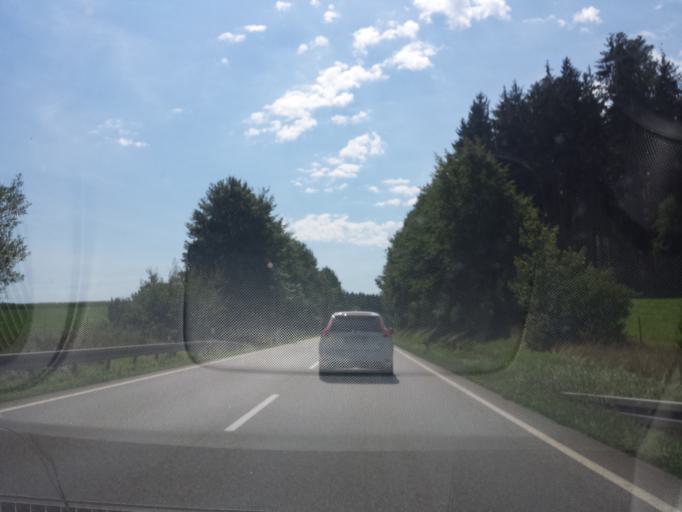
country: DE
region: Bavaria
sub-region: Lower Bavaria
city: Ascha
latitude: 49.0162
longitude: 12.6444
